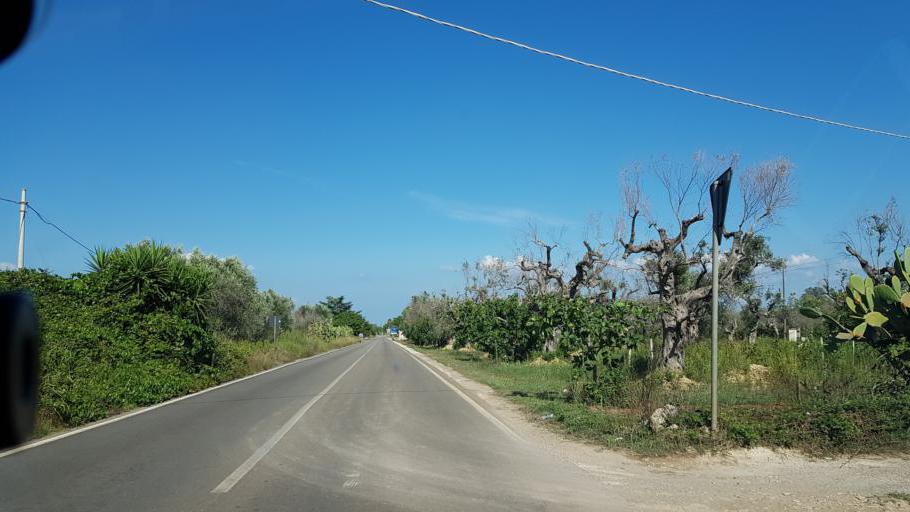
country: IT
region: Apulia
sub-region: Provincia di Lecce
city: San Pietro in Lama
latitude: 40.2993
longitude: 18.1103
